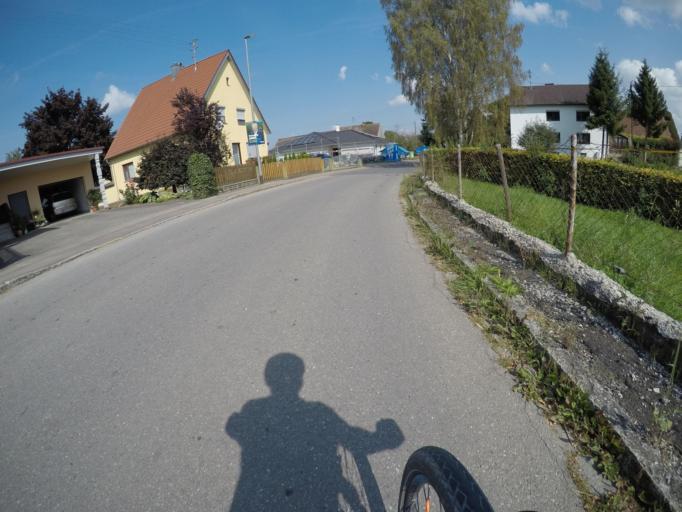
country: DE
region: Bavaria
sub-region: Swabia
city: Nordendorf
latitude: 48.5848
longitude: 10.8245
